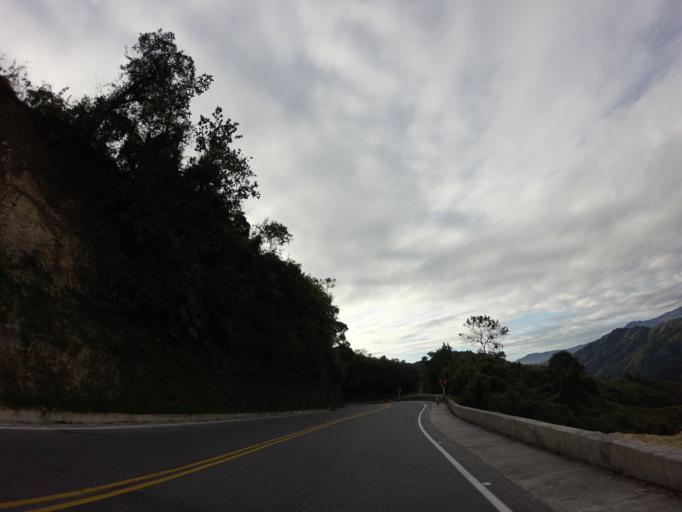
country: CO
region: Tolima
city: Herveo
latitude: 5.1054
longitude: -75.2433
